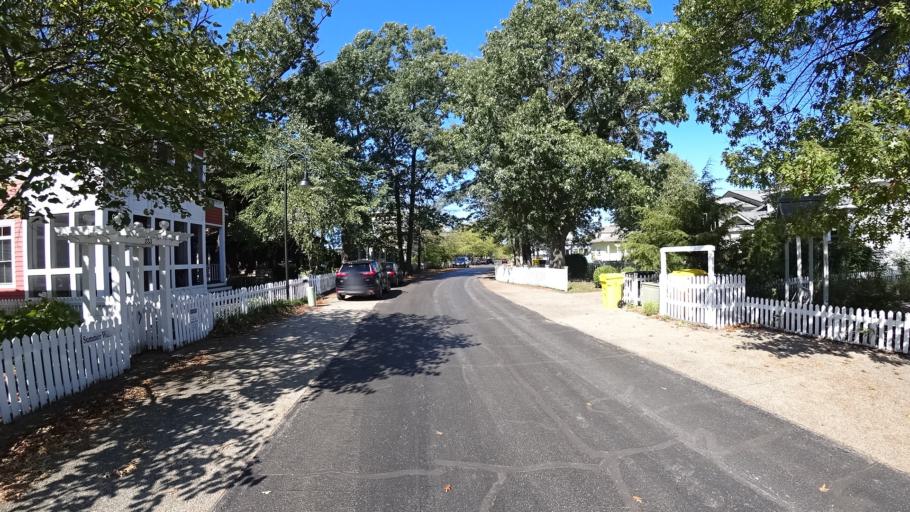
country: US
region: Indiana
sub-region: LaPorte County
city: Michigan City
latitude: 41.7291
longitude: -86.8819
